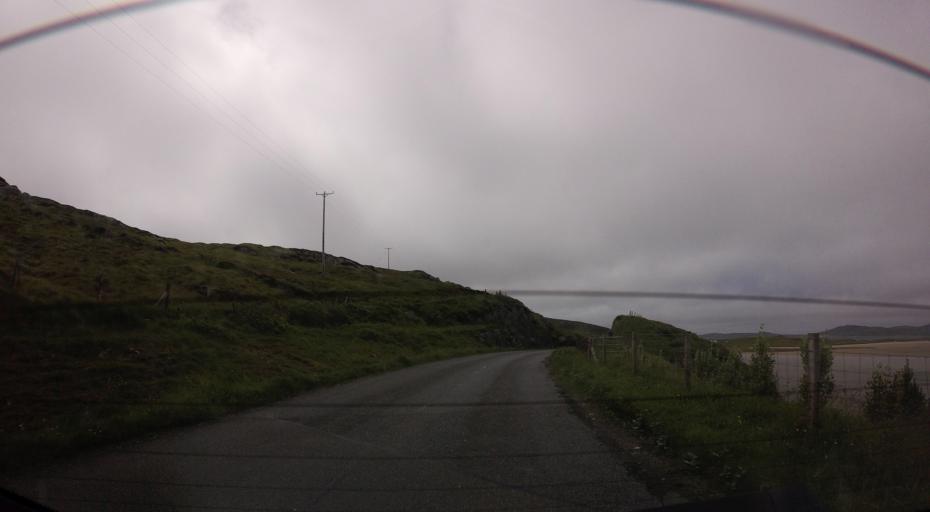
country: GB
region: Scotland
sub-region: Eilean Siar
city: Harris
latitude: 57.8672
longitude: -6.9410
